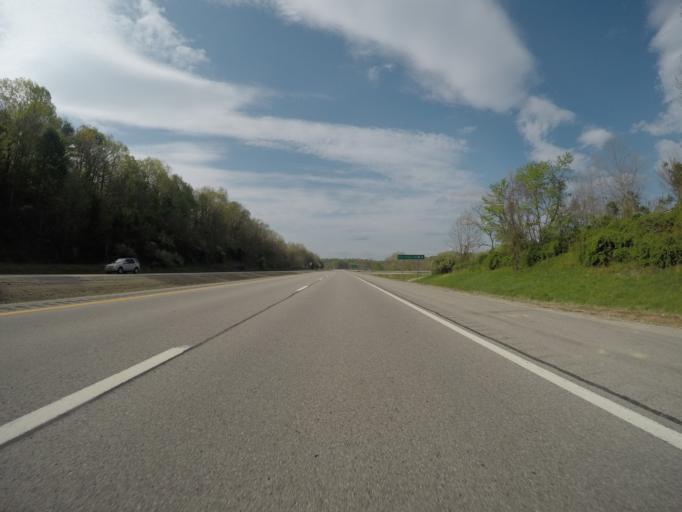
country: US
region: West Virginia
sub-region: Kanawha County
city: Alum Creek
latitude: 38.2440
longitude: -81.8378
